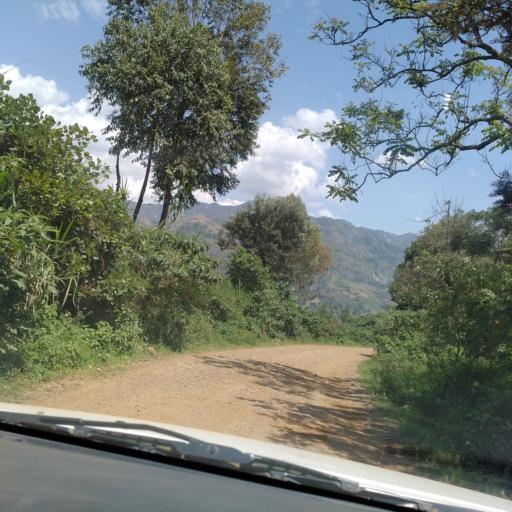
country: RW
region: Western Province
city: Cyangugu
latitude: -2.0655
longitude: 28.9068
